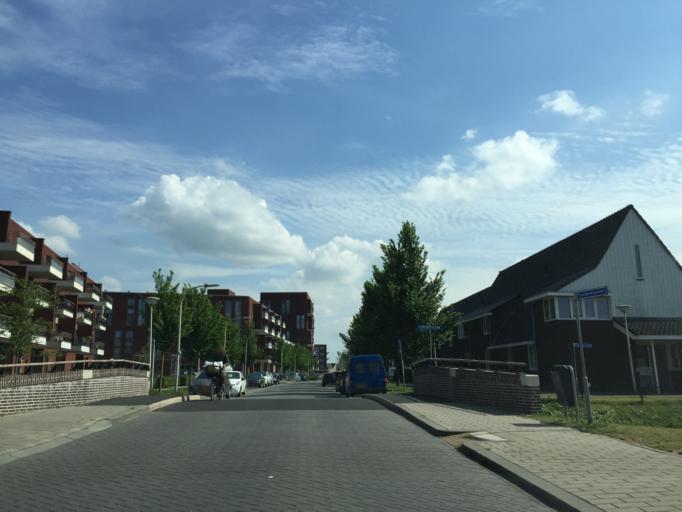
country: NL
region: South Holland
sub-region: Gemeente Pijnacker-Nootdorp
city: Pijnacker
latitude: 52.0064
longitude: 4.4433
